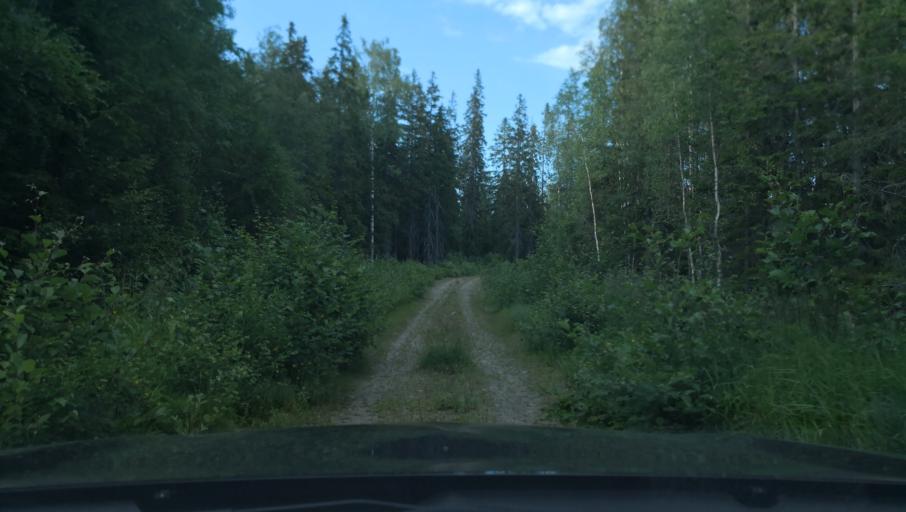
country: SE
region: Dalarna
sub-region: Ludvika Kommun
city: Ludvika
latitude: 60.0783
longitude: 15.2955
